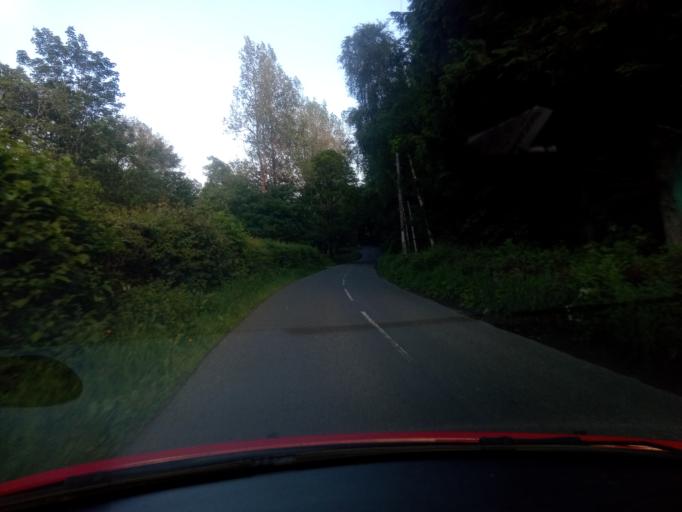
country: GB
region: Scotland
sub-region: The Scottish Borders
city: Selkirk
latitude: 55.5306
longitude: -2.9069
